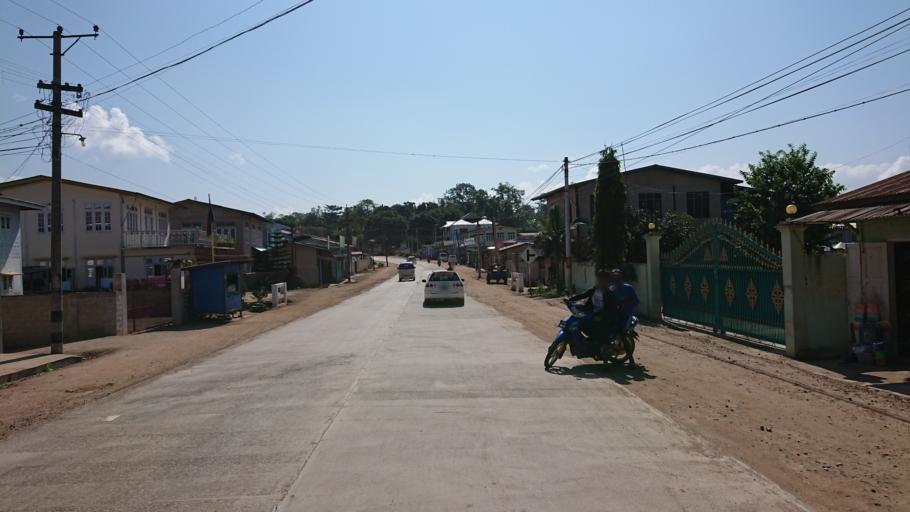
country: MM
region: Shan
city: Taunggyi
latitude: 20.8017
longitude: 97.1788
